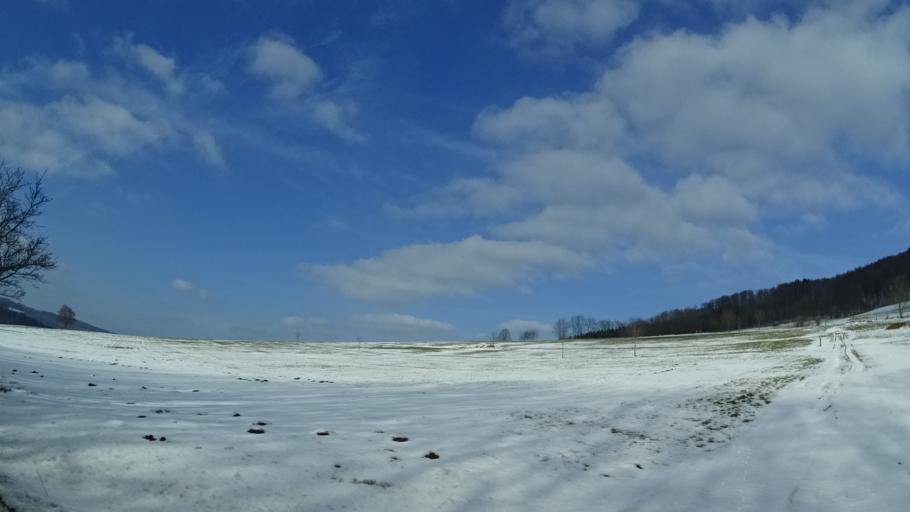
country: DE
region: Thuringia
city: Birx
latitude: 50.5254
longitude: 10.0262
